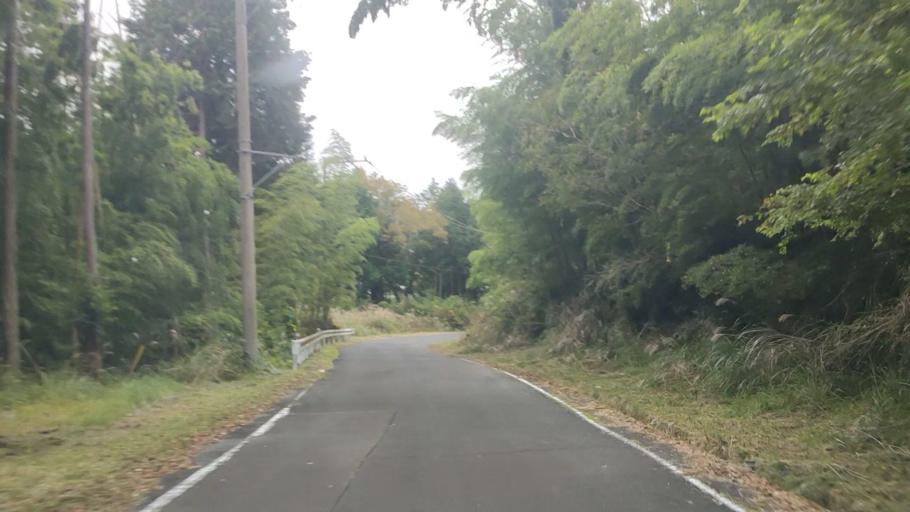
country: JP
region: Shizuoka
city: Ito
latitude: 34.9224
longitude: 138.9853
